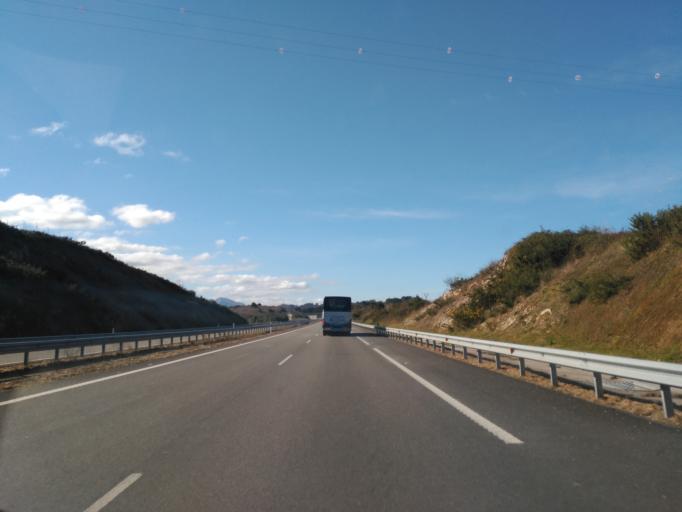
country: ES
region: Asturias
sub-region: Province of Asturias
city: Llanes
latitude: 43.4015
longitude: -4.6733
